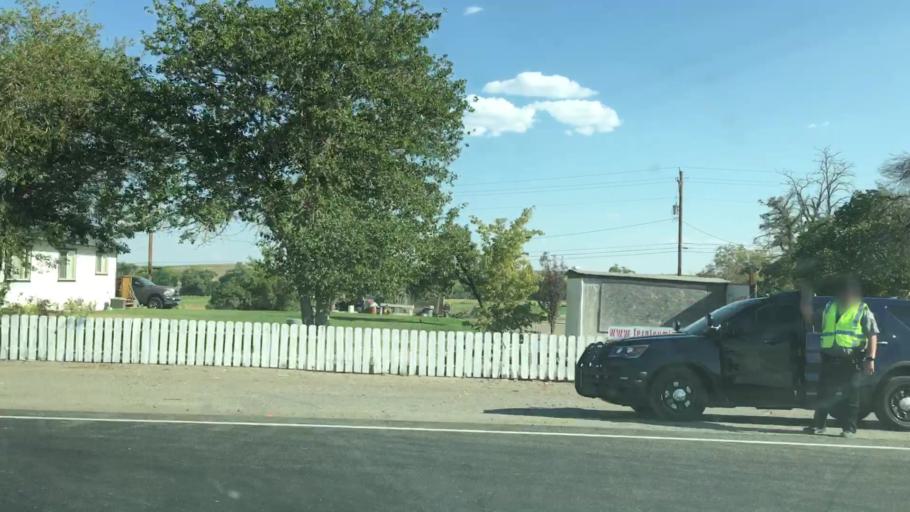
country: US
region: Nevada
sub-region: Lyon County
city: Fernley
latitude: 39.6305
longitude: -119.2905
